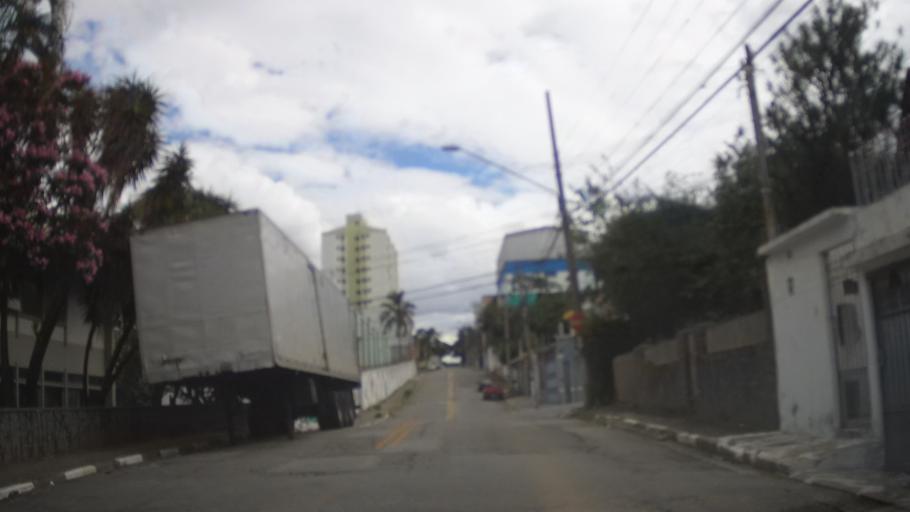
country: BR
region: Sao Paulo
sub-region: Guarulhos
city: Guarulhos
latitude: -23.4797
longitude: -46.5498
